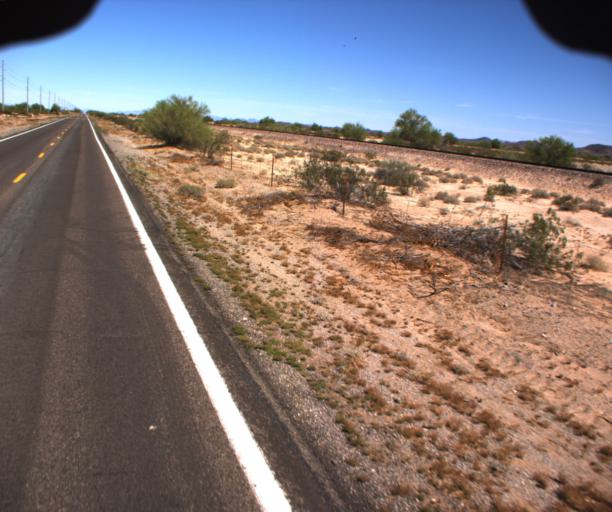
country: US
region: Arizona
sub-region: La Paz County
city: Salome
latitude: 33.8720
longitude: -113.9335
